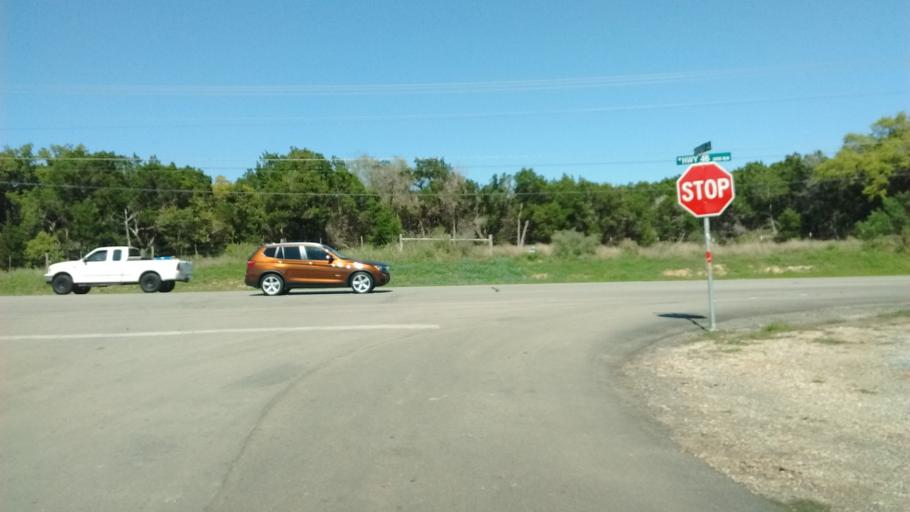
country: US
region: Texas
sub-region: Comal County
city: New Braunfels
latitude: 29.7286
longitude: -98.1904
